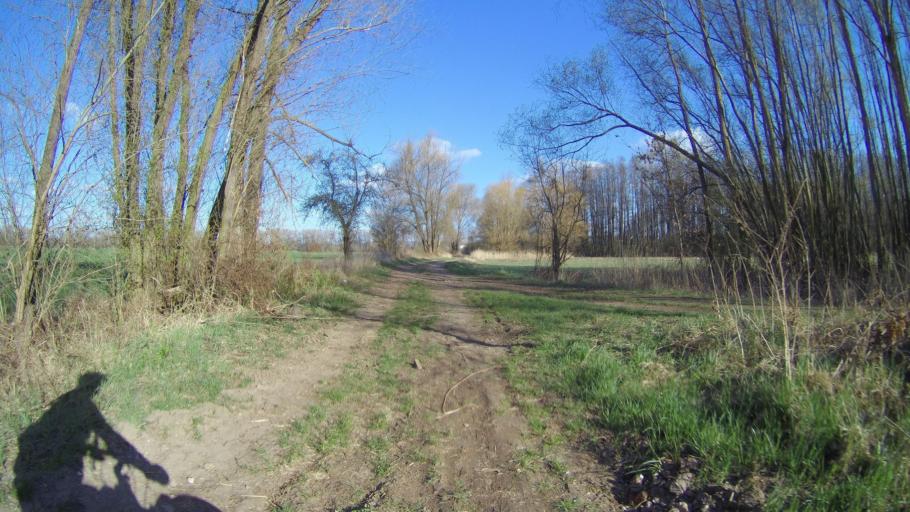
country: CZ
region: Ustecky
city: Zatec
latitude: 50.3348
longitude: 13.5873
